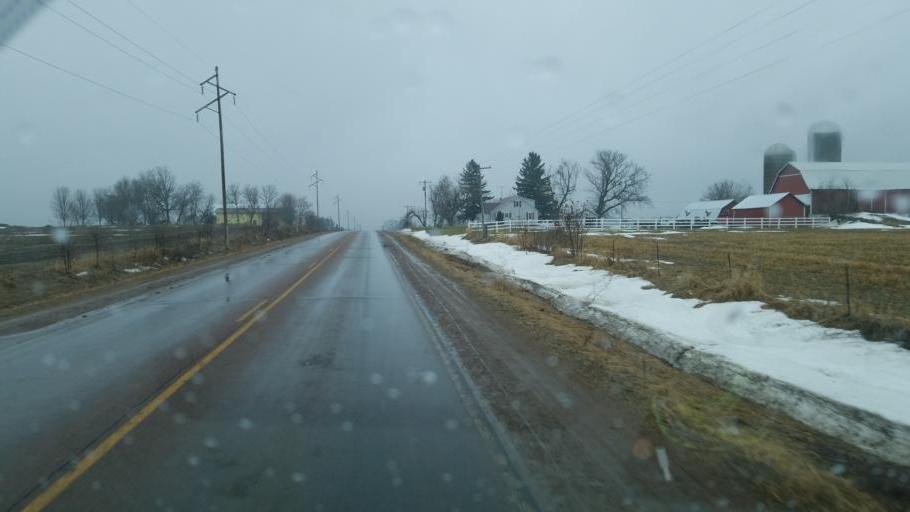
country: US
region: Wisconsin
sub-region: Clark County
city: Neillsville
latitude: 44.5607
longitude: -90.3961
